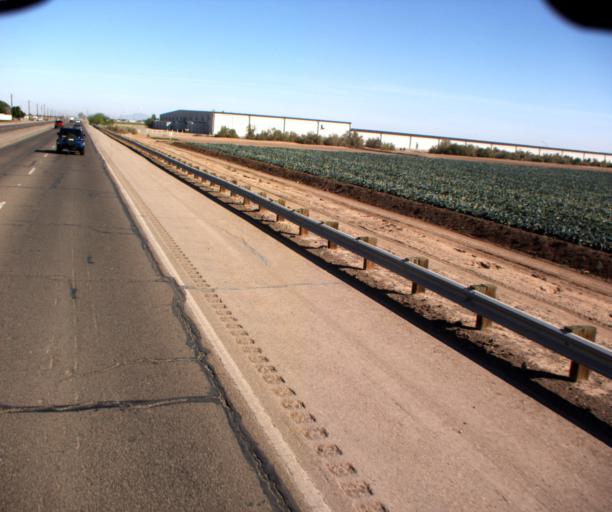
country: US
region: Arizona
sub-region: Yuma County
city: San Luis
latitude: 32.5259
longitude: -114.7866
